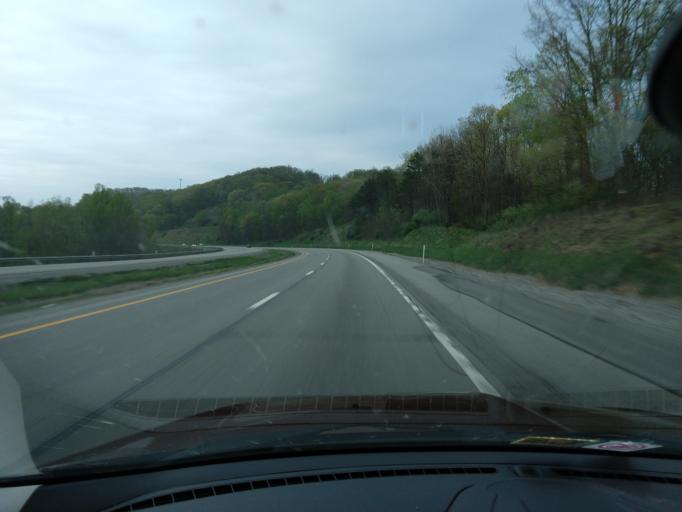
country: US
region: West Virginia
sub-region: Lewis County
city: Weston
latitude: 38.9208
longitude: -80.5531
